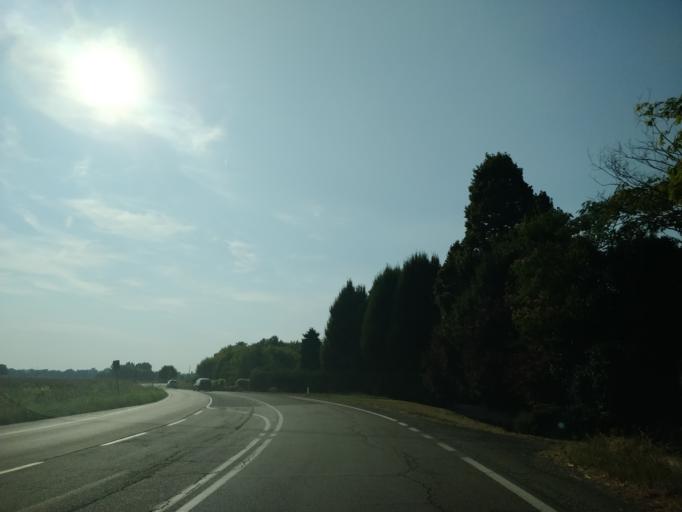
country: IT
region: Emilia-Romagna
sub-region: Provincia di Bologna
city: Argelato
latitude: 44.6567
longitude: 11.3228
